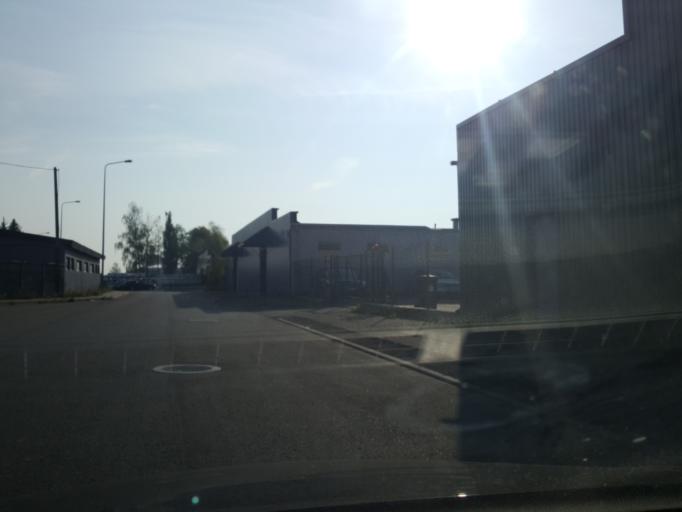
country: LT
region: Alytaus apskritis
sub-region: Alytus
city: Alytus
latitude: 54.4368
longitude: 24.0201
